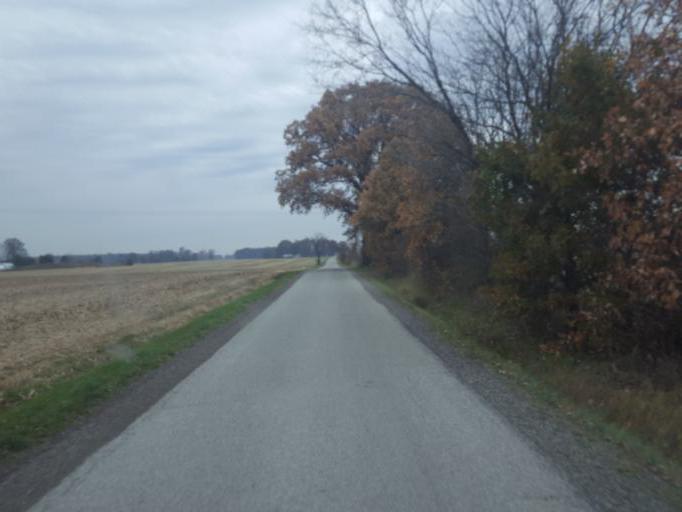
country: US
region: Ohio
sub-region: Marion County
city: Marion
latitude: 40.5096
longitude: -83.1180
